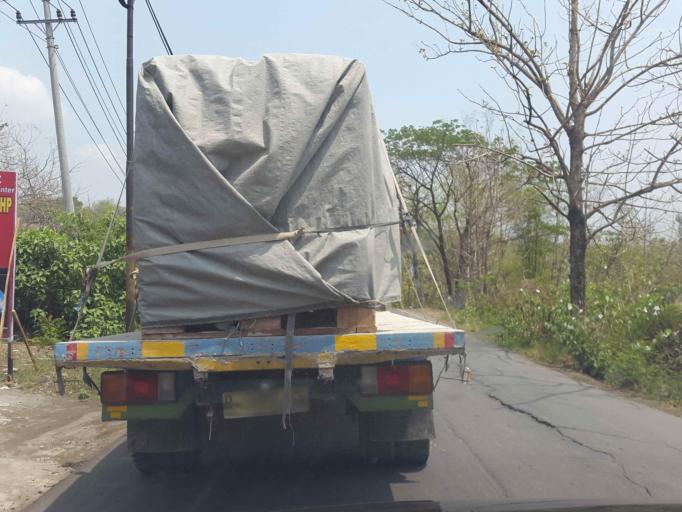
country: ID
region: Central Java
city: Surakarta
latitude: -7.5245
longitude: 110.8490
